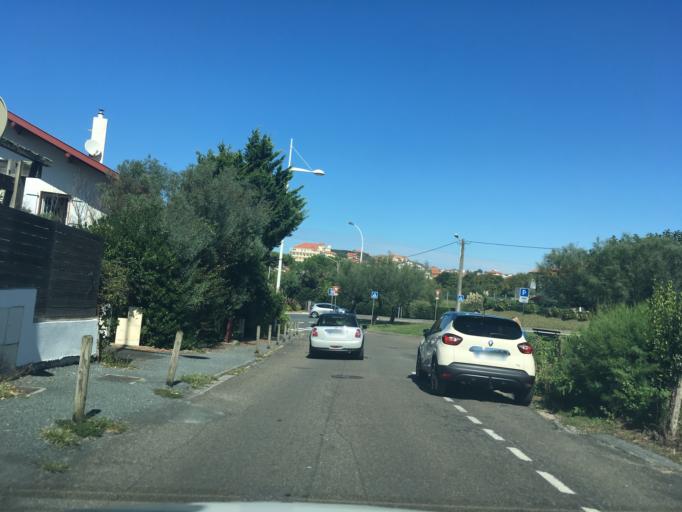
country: FR
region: Aquitaine
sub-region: Departement des Pyrenees-Atlantiques
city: Biarritz
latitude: 43.4645
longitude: -1.5719
